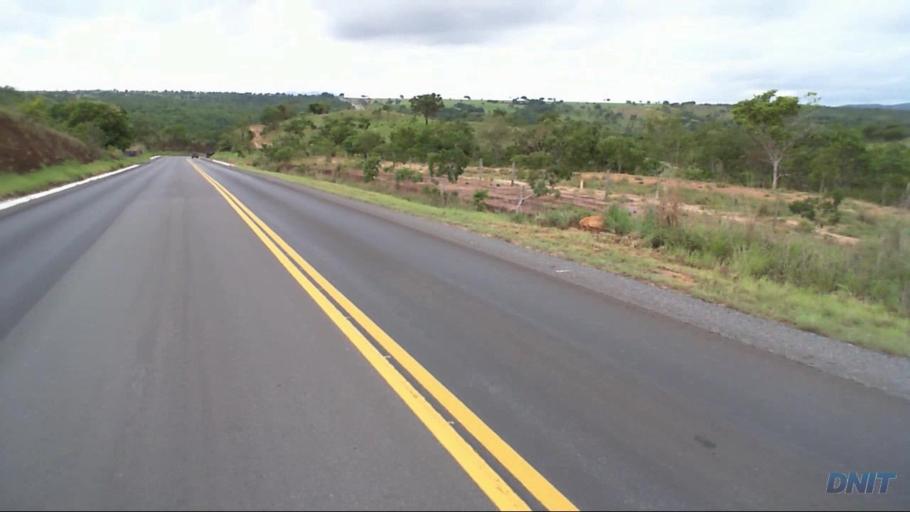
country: BR
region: Goias
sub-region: Padre Bernardo
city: Padre Bernardo
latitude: -15.2141
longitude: -48.5787
